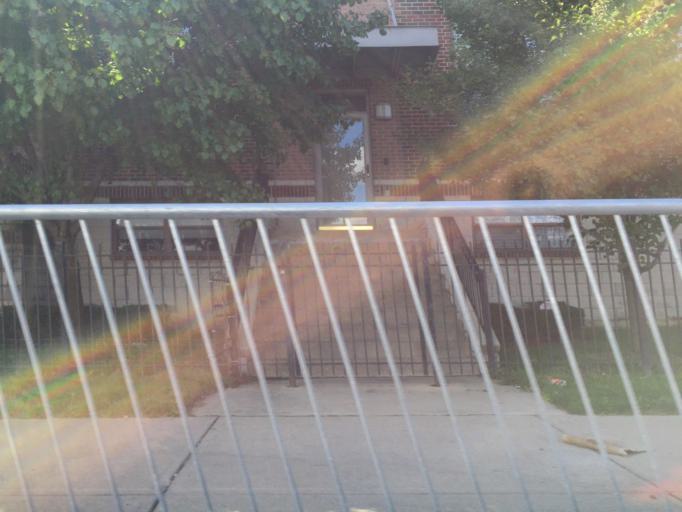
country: US
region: Michigan
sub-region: Wayne County
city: Hamtramck
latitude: 42.3738
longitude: -83.0758
